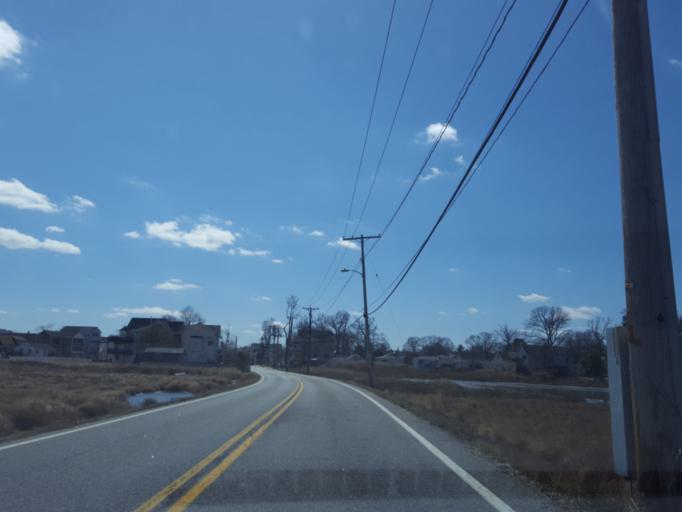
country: US
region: Maryland
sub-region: Calvert County
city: North Beach
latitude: 38.7124
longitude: -76.5305
